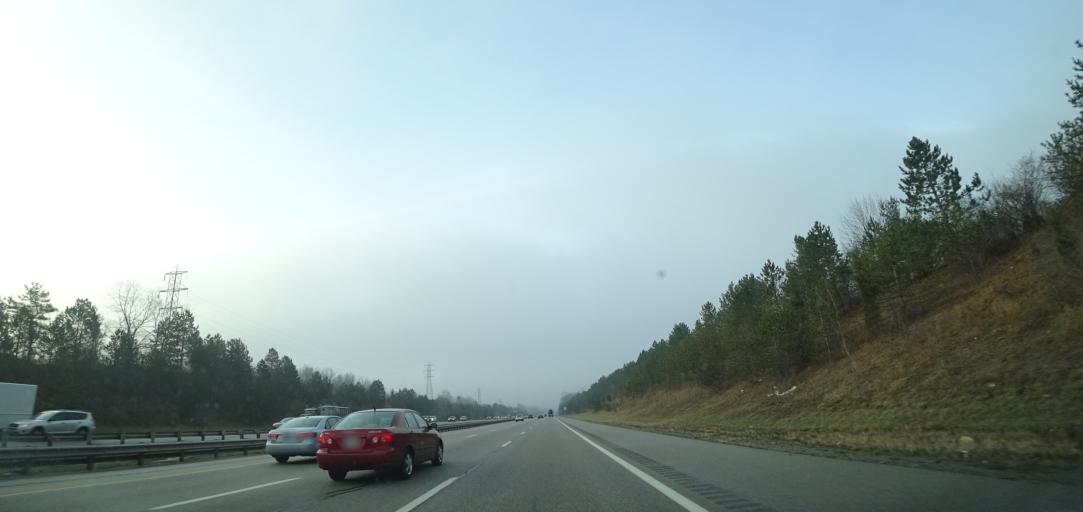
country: US
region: Ohio
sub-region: Cuyahoga County
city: Brecksville
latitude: 41.3369
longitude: -81.6497
